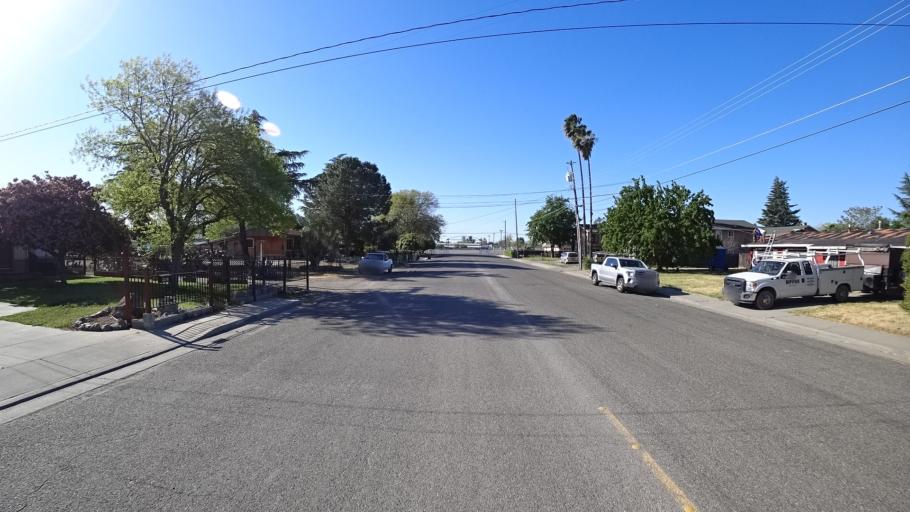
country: US
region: California
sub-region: Glenn County
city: Orland
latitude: 39.7448
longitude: -122.1822
